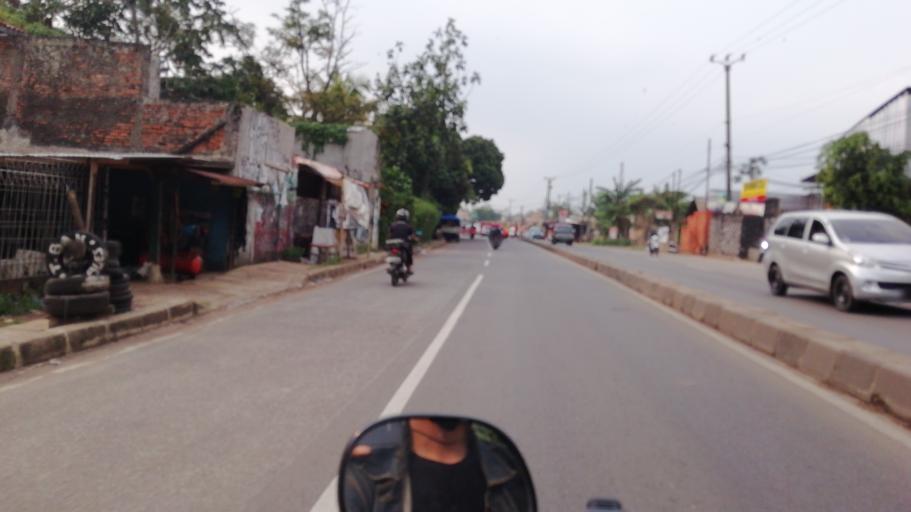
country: ID
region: West Java
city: Parung
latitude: -6.4780
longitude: 106.7309
